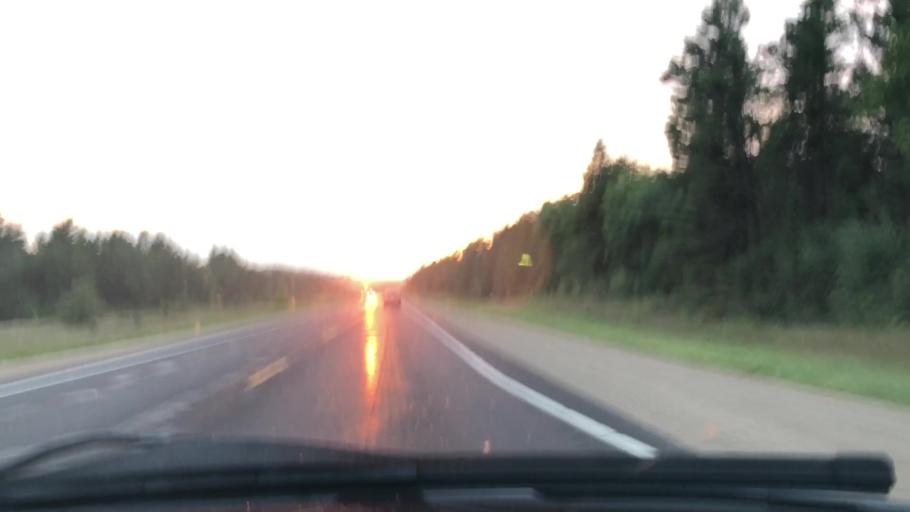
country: US
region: Wisconsin
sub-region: Richland County
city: Richland Center
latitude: 43.2137
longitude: -90.2778
